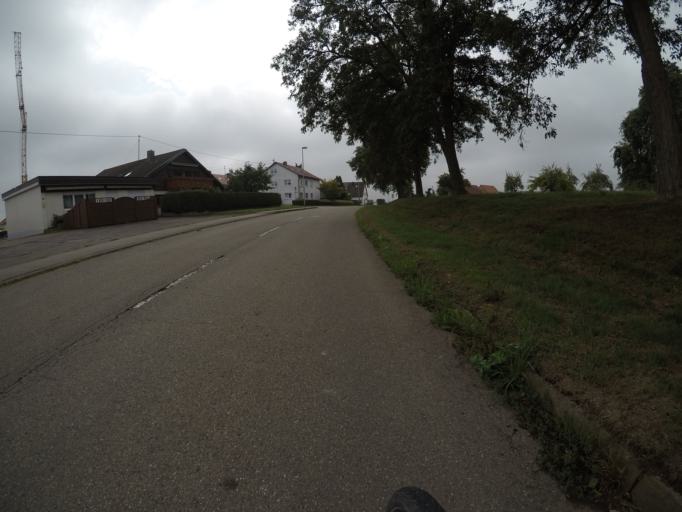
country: DE
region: Baden-Wuerttemberg
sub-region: Regierungsbezirk Stuttgart
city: Herrenberg
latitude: 48.6088
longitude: 8.8372
